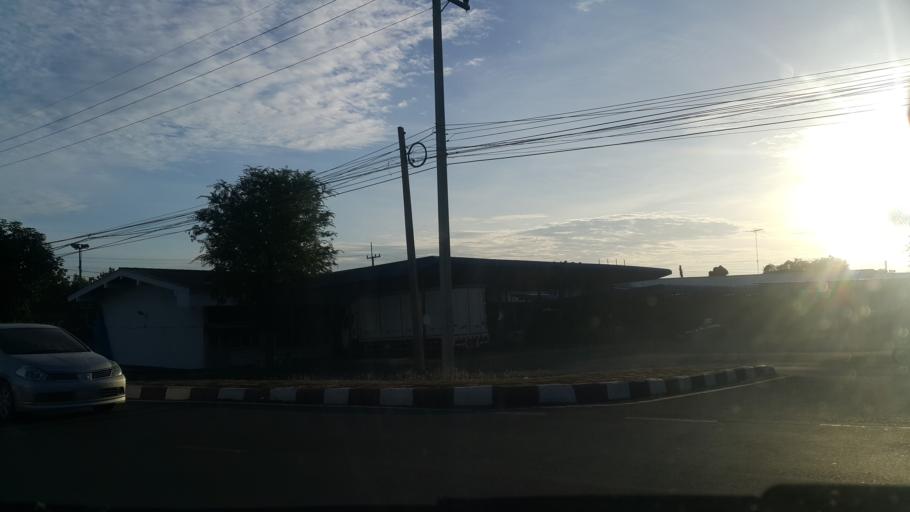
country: TH
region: Chon Buri
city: Sattahip
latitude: 12.6658
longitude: 100.9186
